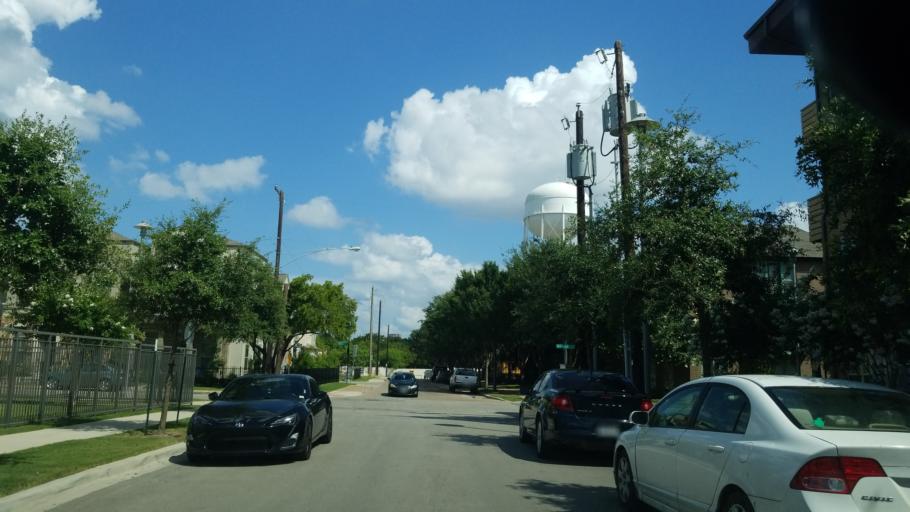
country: US
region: Texas
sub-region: Dallas County
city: Highland Park
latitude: 32.8269
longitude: -96.8194
